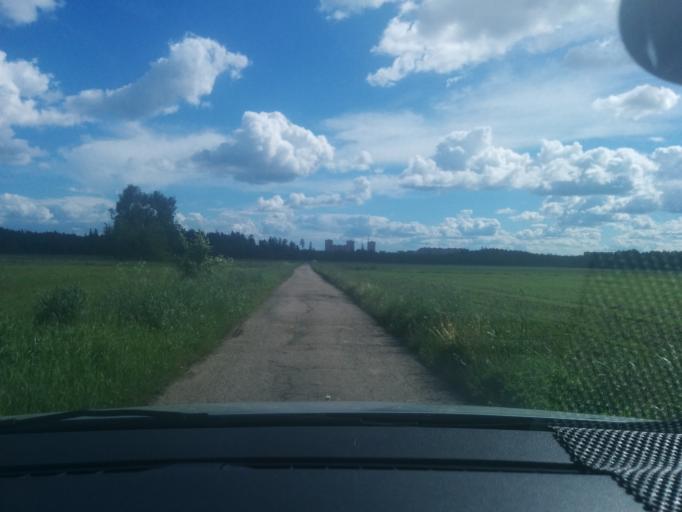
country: RU
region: Moskovskaya
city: Lugovaya
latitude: 56.0445
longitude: 37.4978
